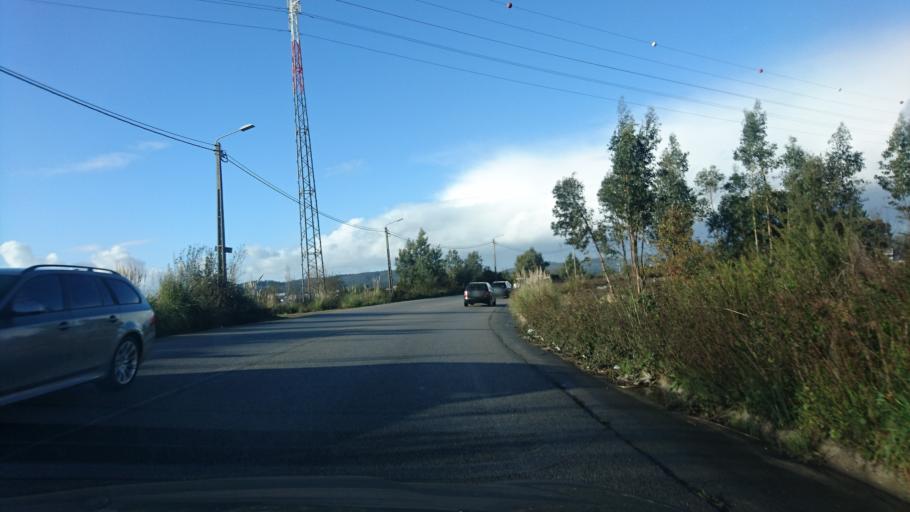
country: PT
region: Porto
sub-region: Valongo
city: Campo
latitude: 41.1808
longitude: -8.4490
